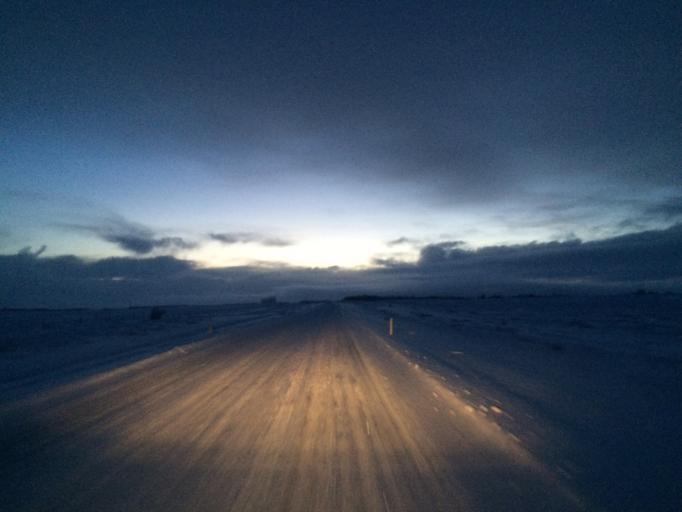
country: IS
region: South
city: Selfoss
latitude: 64.0876
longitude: -20.7394
